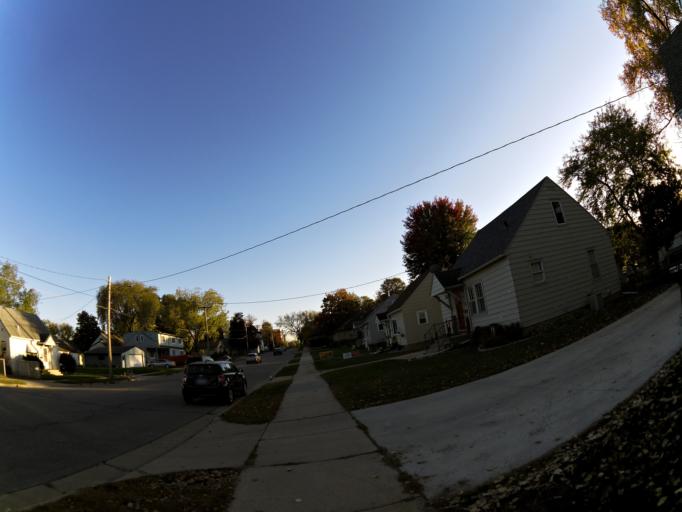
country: US
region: Minnesota
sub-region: Olmsted County
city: Rochester
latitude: 44.0346
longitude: -92.4684
